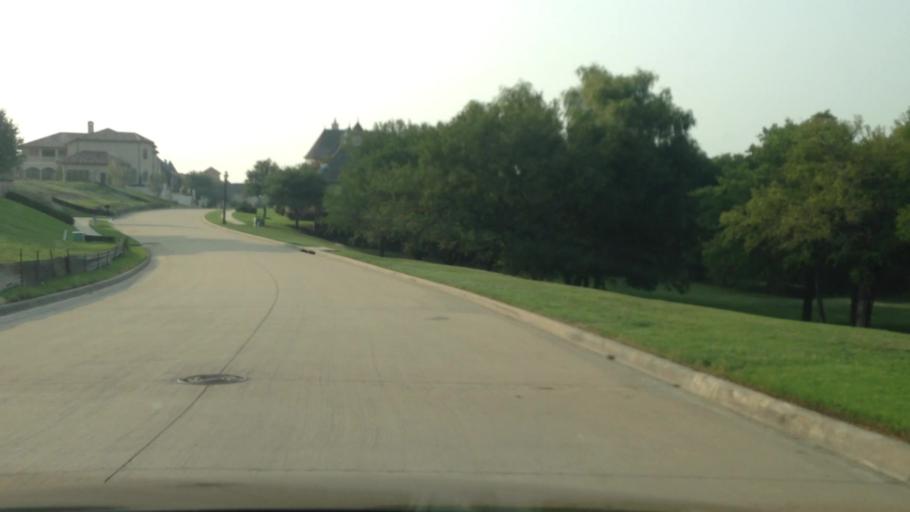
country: US
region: Texas
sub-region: Collin County
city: Frisco
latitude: 33.1233
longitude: -96.8358
